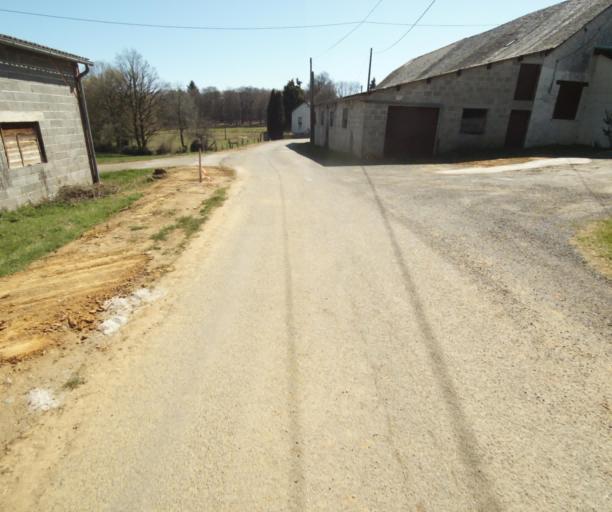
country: FR
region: Limousin
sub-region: Departement de la Correze
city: Saint-Clement
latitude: 45.3737
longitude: 1.6809
